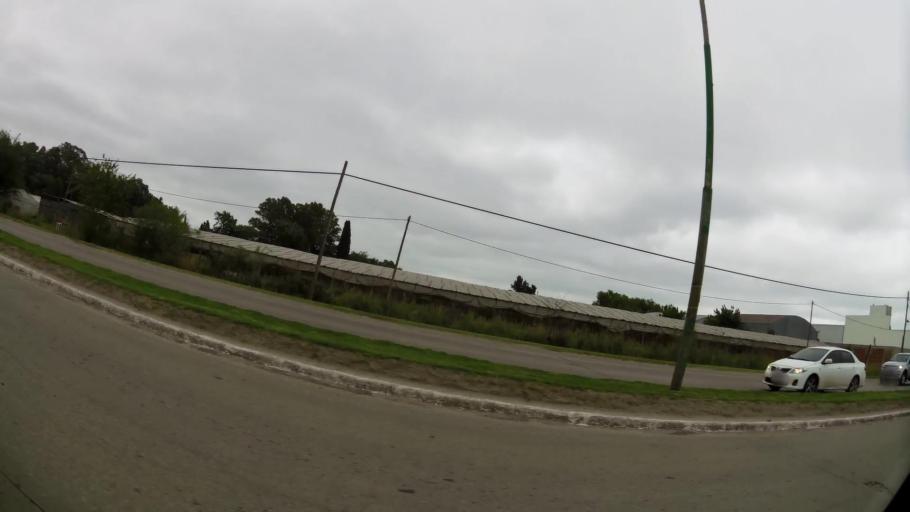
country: AR
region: Buenos Aires
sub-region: Partido de La Plata
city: La Plata
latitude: -35.0218
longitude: -58.0773
